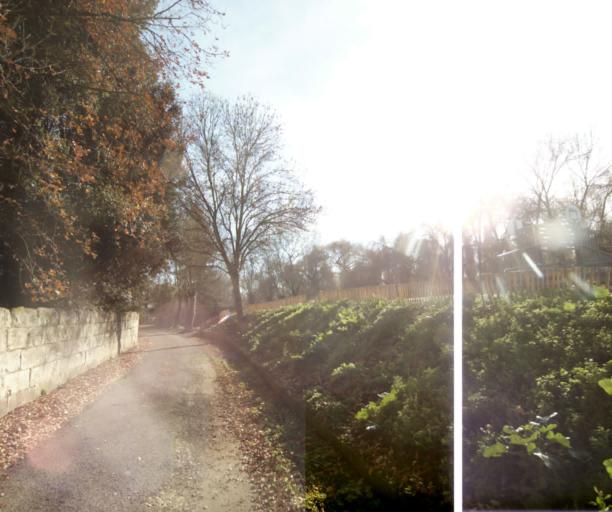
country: FR
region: Poitou-Charentes
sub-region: Departement de la Charente-Maritime
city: Chaniers
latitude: 45.7172
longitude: -0.5599
